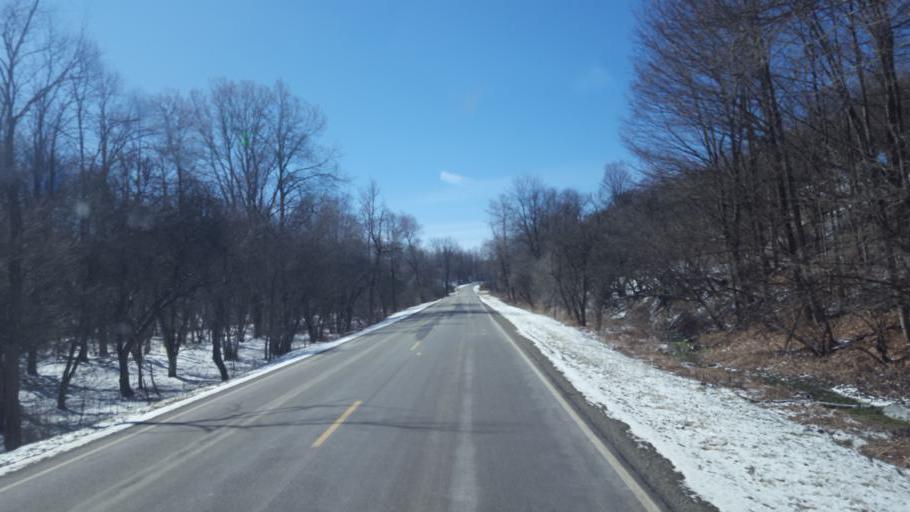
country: US
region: New York
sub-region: Allegany County
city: Andover
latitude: 42.0072
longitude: -77.7629
